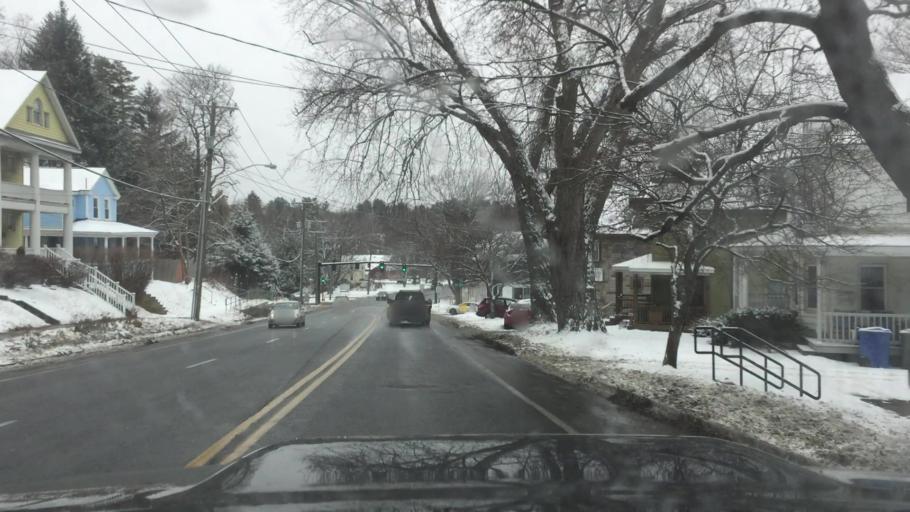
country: US
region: Massachusetts
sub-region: Berkshire County
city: Pittsfield
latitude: 42.4395
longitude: -73.2570
